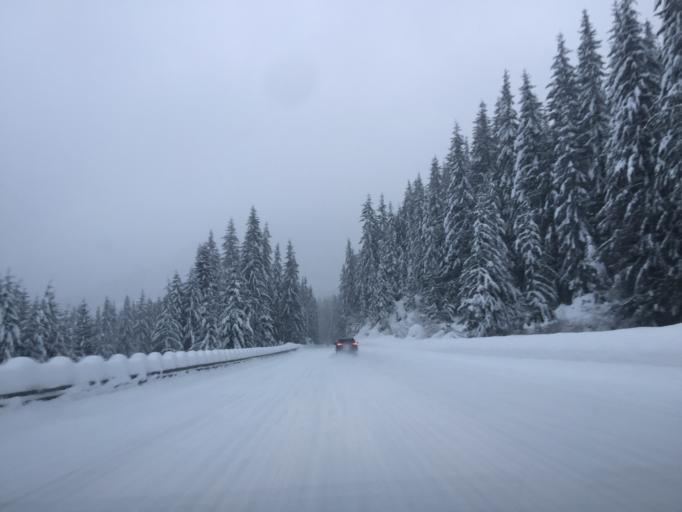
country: US
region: Washington
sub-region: Chelan County
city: Leavenworth
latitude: 47.7813
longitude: -121.0265
